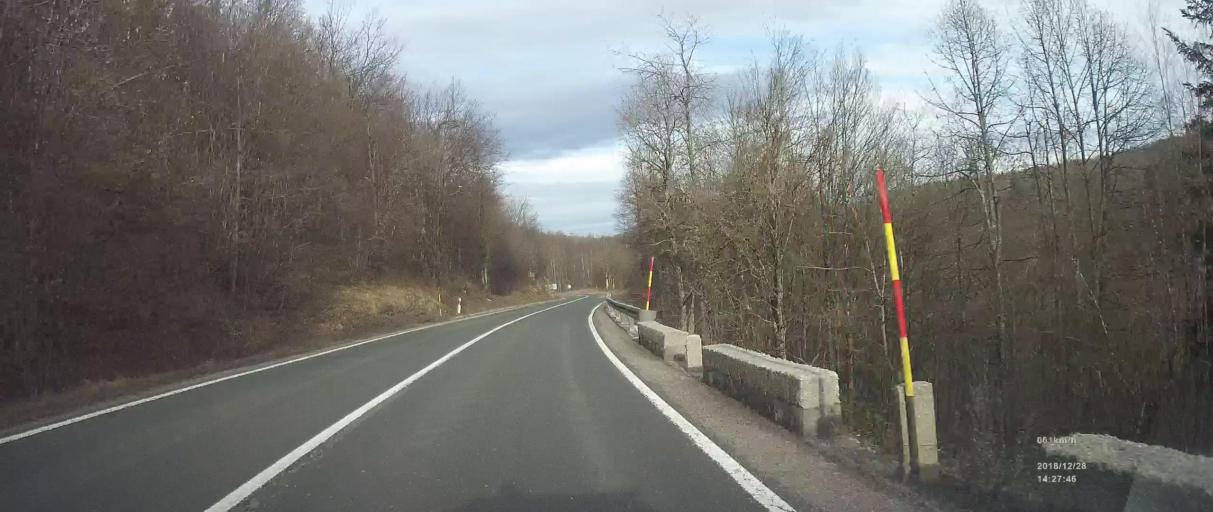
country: HR
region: Primorsko-Goranska
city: Vrbovsko
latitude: 45.4046
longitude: 15.1088
